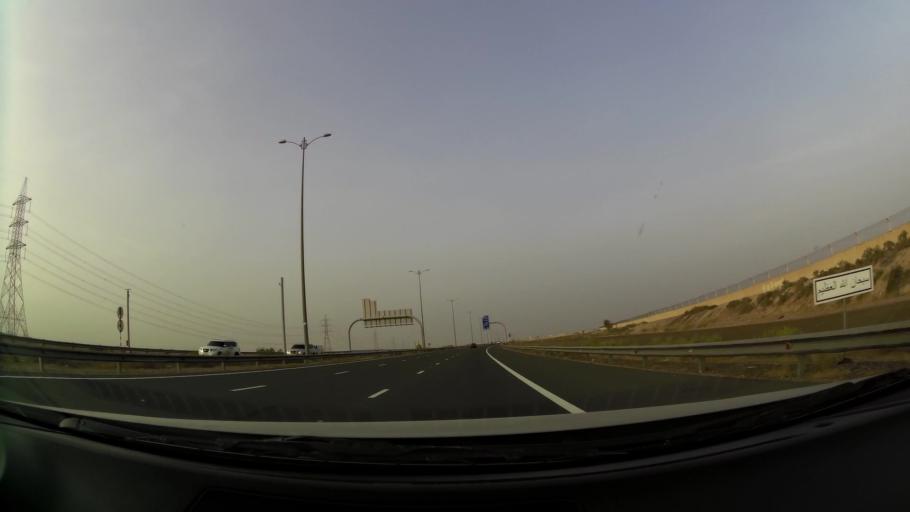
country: OM
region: Al Buraimi
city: Al Buraymi
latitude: 24.3322
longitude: 55.7636
